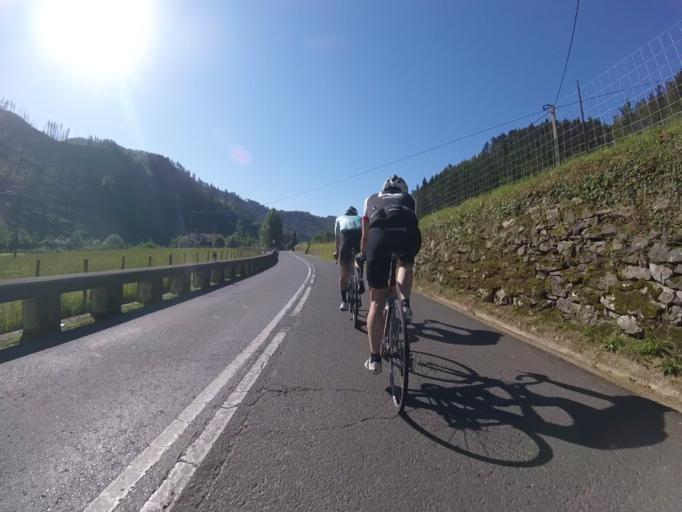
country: ES
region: Basque Country
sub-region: Provincia de Guipuzcoa
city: Azpeitia
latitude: 43.1526
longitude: -2.2404
